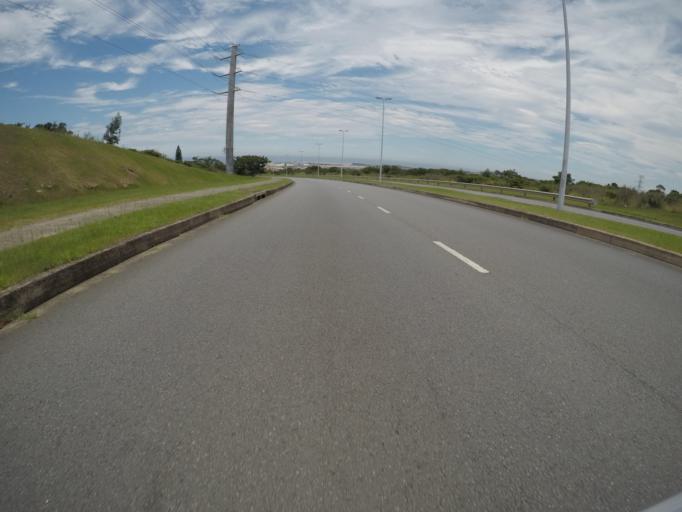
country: ZA
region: Eastern Cape
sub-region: Buffalo City Metropolitan Municipality
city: East London
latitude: -33.0381
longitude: 27.8471
